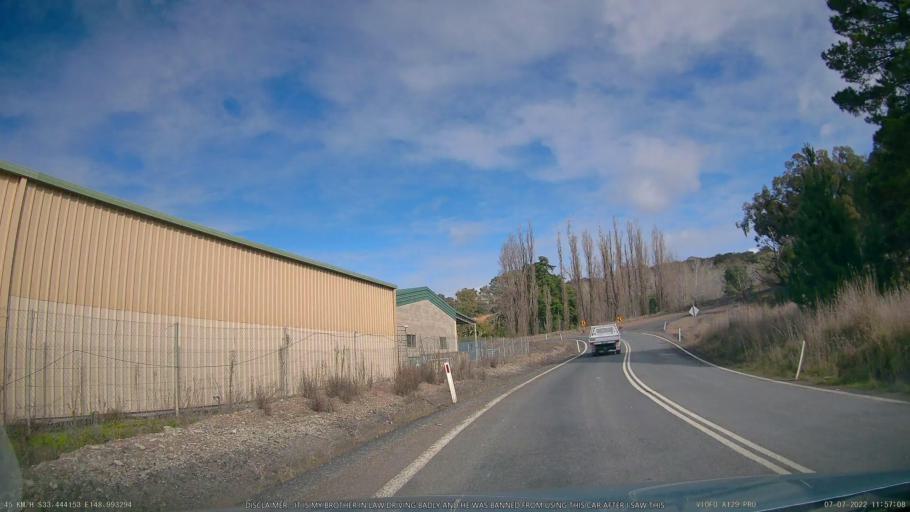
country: AU
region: New South Wales
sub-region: Blayney
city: Millthorpe
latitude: -33.4443
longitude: 148.9930
